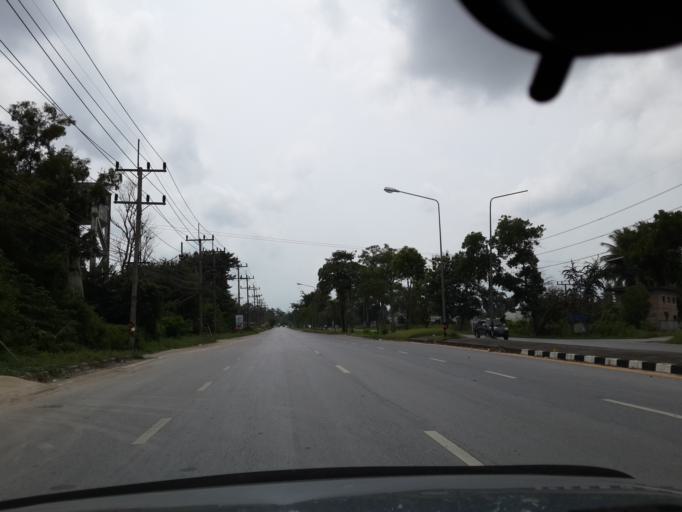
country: TH
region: Pattani
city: Pattani
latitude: 6.8614
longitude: 101.2704
